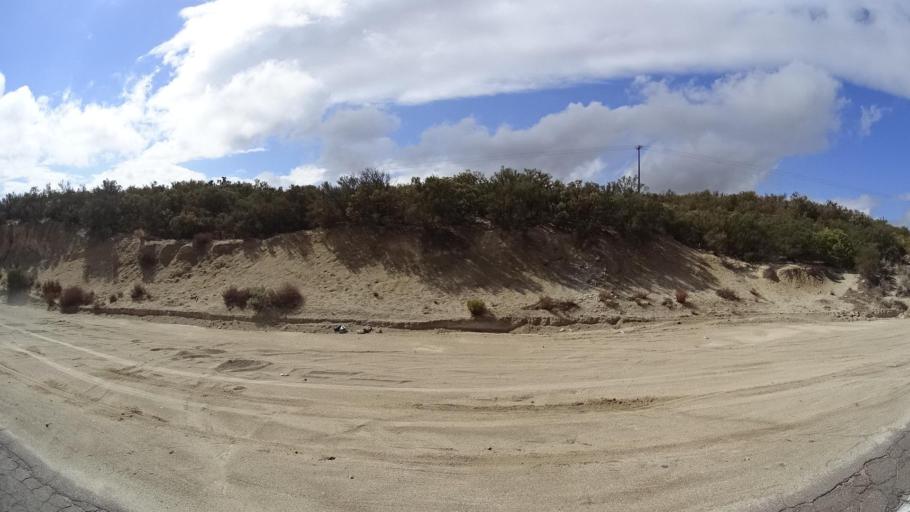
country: US
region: California
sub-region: San Diego County
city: Campo
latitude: 32.6967
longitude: -116.3489
